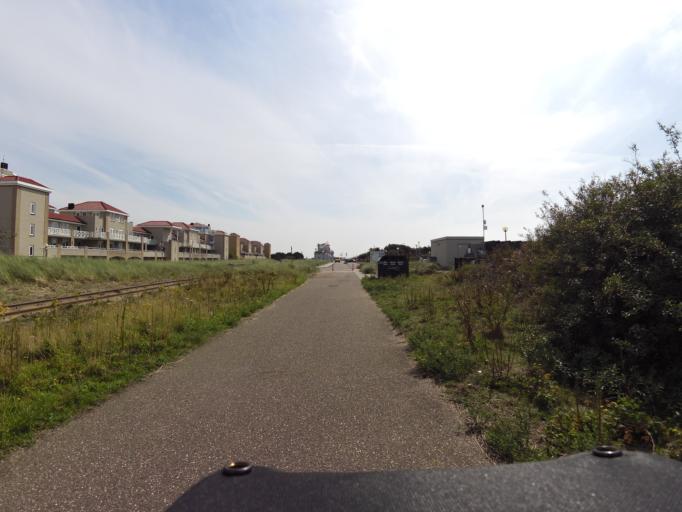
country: NL
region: Zeeland
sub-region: Schouwen-Duiveland
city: Scharendijke
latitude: 51.7601
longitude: 3.8555
